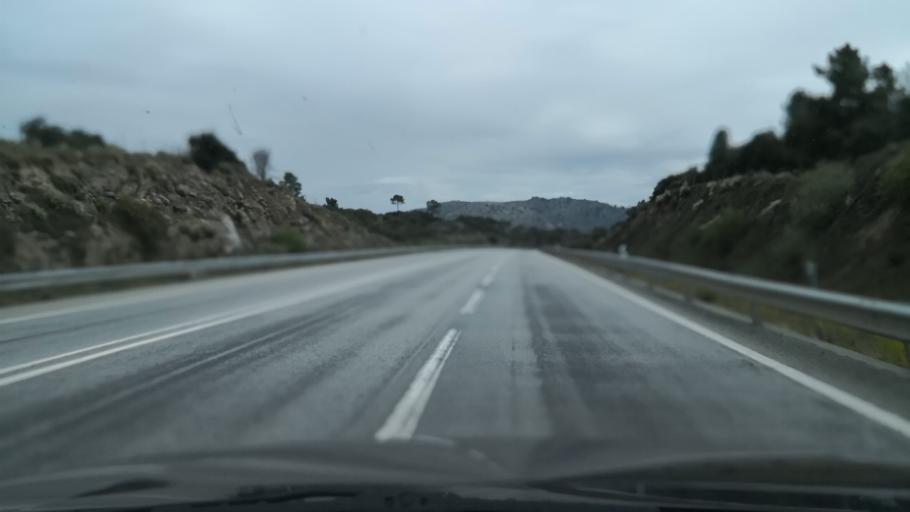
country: PT
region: Guarda
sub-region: Celorico da Beira
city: Celorico da Beira
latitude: 40.6310
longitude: -7.3111
